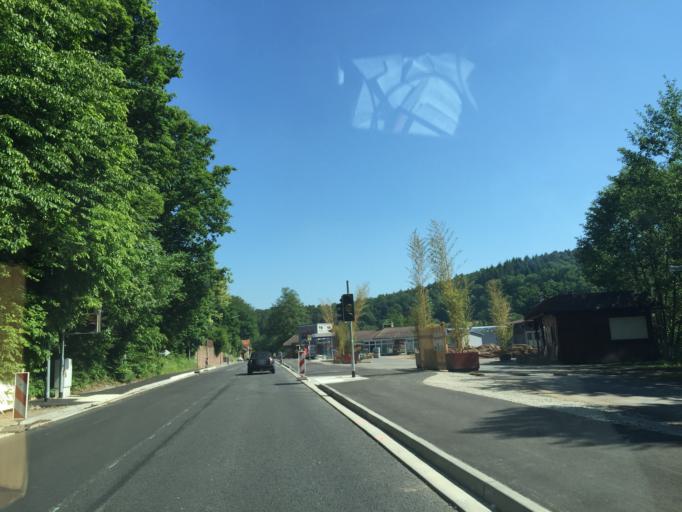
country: DE
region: Hesse
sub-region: Regierungsbezirk Darmstadt
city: Erbach
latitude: 49.6173
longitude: 8.9934
